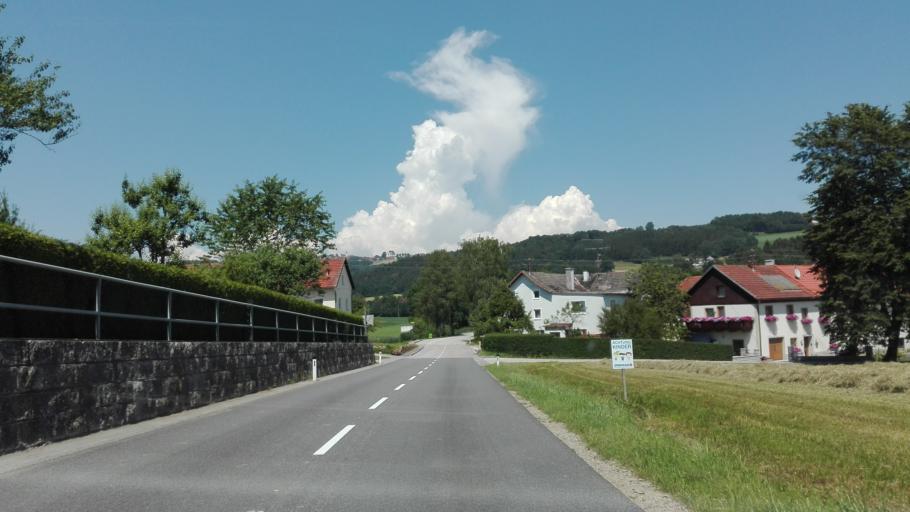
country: AT
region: Upper Austria
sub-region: Politischer Bezirk Grieskirchen
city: Grieskirchen
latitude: 48.3585
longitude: 13.8620
